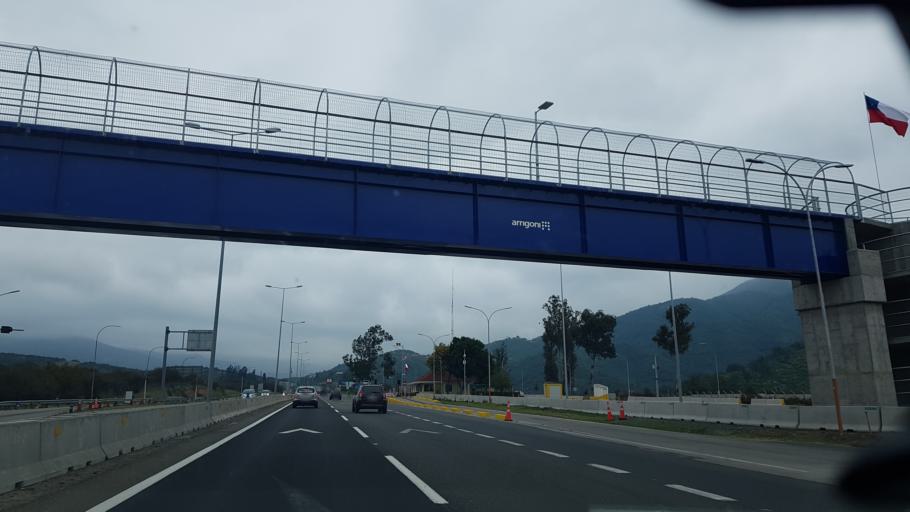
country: CL
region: Santiago Metropolitan
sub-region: Provincia de Melipilla
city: Melipilla
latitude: -33.4079
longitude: -71.1800
